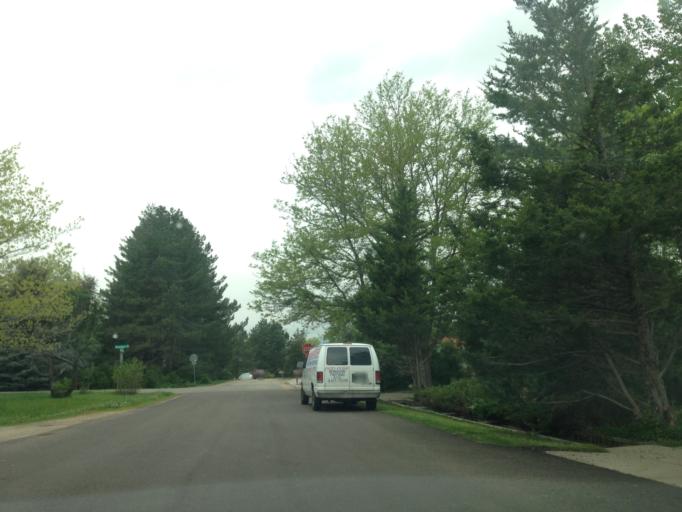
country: US
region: Colorado
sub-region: Boulder County
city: Louisville
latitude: 40.0068
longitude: -105.1734
